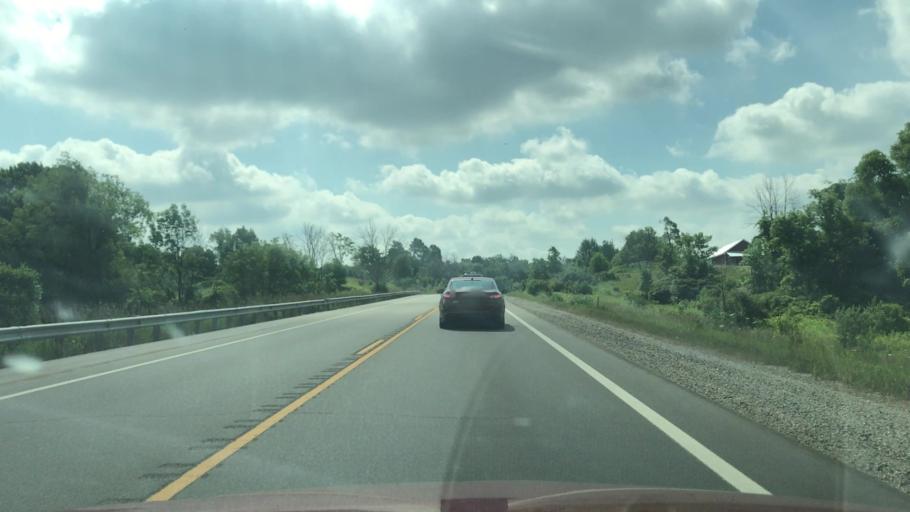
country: US
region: Michigan
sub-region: Kent County
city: Kent City
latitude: 43.2004
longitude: -85.7288
